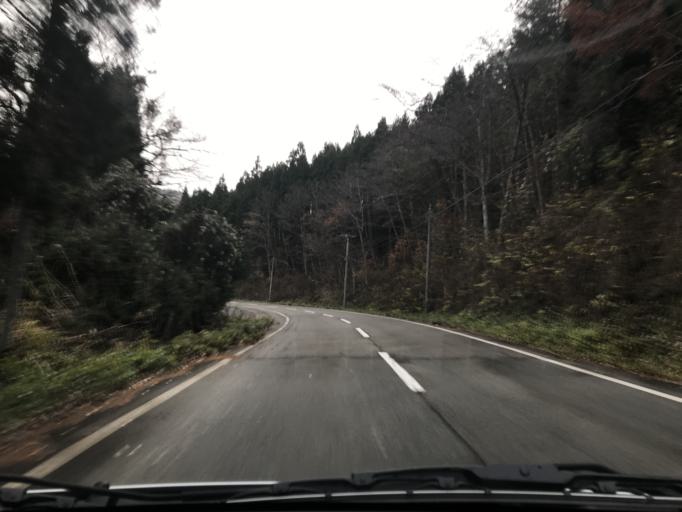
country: JP
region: Iwate
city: Tono
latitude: 39.1788
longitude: 141.3624
